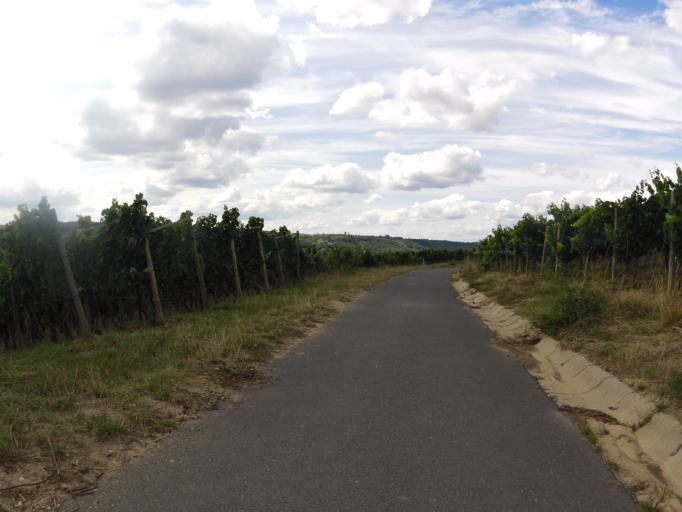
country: DE
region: Bavaria
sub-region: Regierungsbezirk Unterfranken
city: Sommerhausen
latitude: 49.6981
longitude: 10.0334
